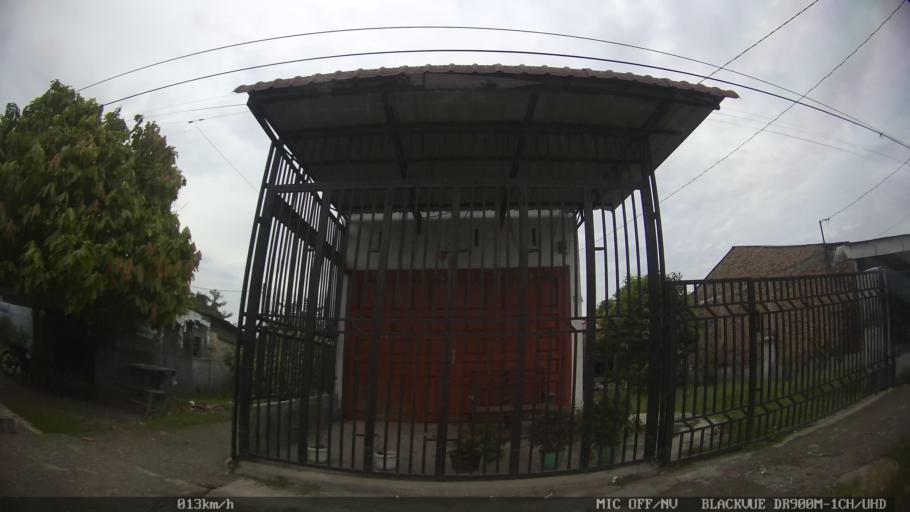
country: ID
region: North Sumatra
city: Sunggal
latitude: 3.6215
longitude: 98.5956
